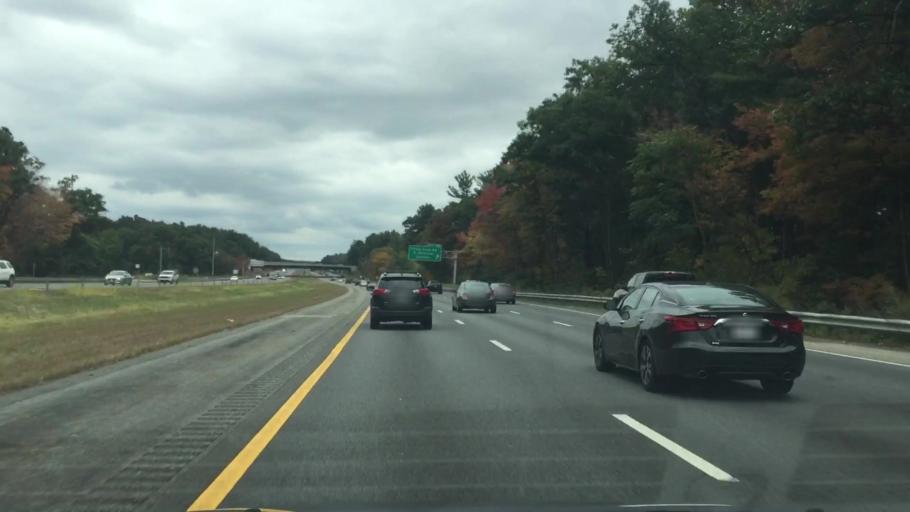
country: US
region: Massachusetts
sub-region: Middlesex County
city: Billerica
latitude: 42.5650
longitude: -71.3009
